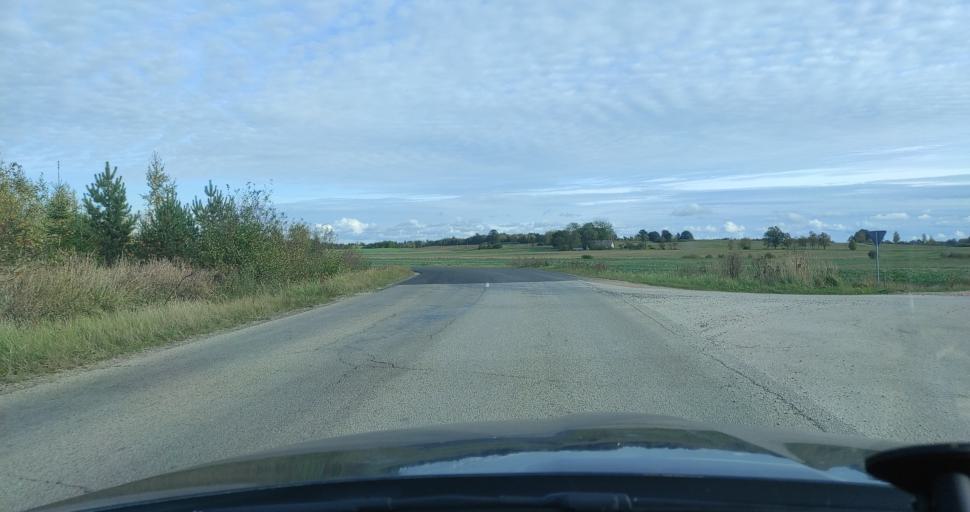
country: LV
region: Jaunpils
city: Jaunpils
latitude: 56.7003
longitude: 22.9849
